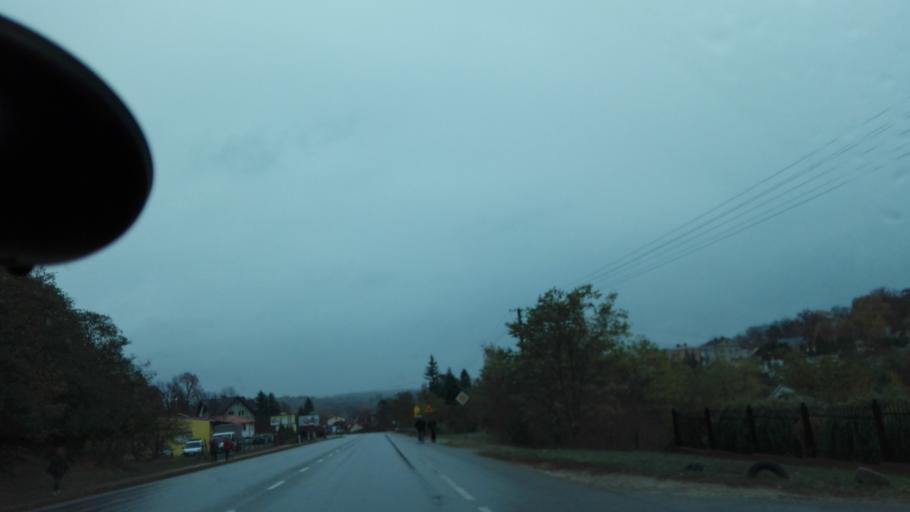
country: PL
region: Lublin Voivodeship
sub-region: Powiat pulawski
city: Pulawy
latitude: 51.4097
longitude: 21.9273
